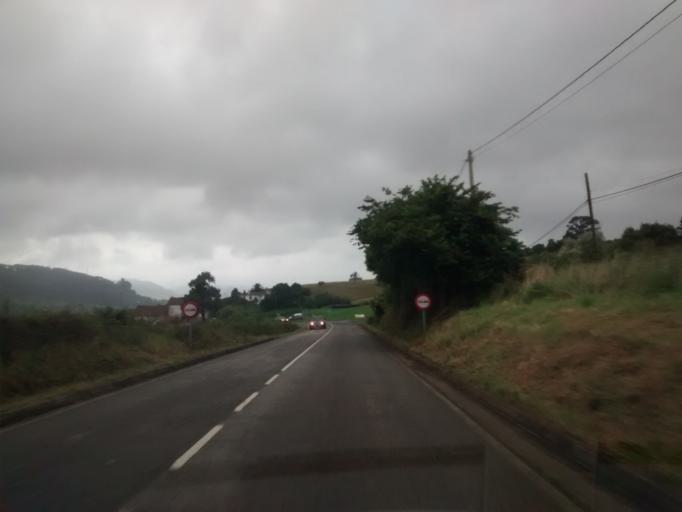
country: ES
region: Asturias
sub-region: Province of Asturias
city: Villaviciosa
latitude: 43.5019
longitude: -5.4262
